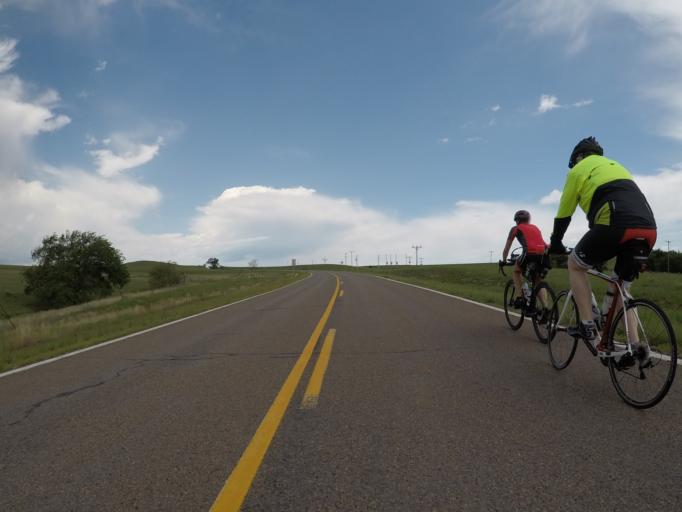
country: US
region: Kansas
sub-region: Wabaunsee County
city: Alma
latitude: 38.8691
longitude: -96.3144
